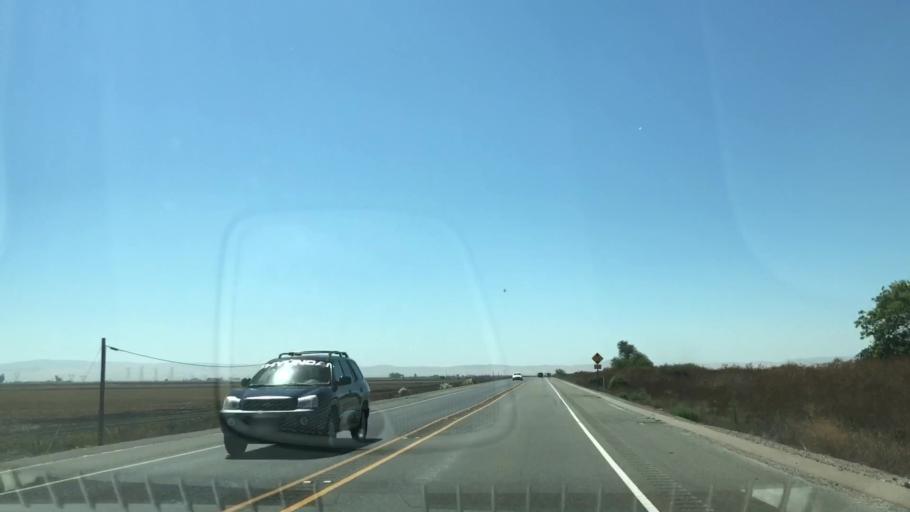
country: US
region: California
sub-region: San Joaquin County
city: Country Club
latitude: 37.9081
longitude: -121.4567
